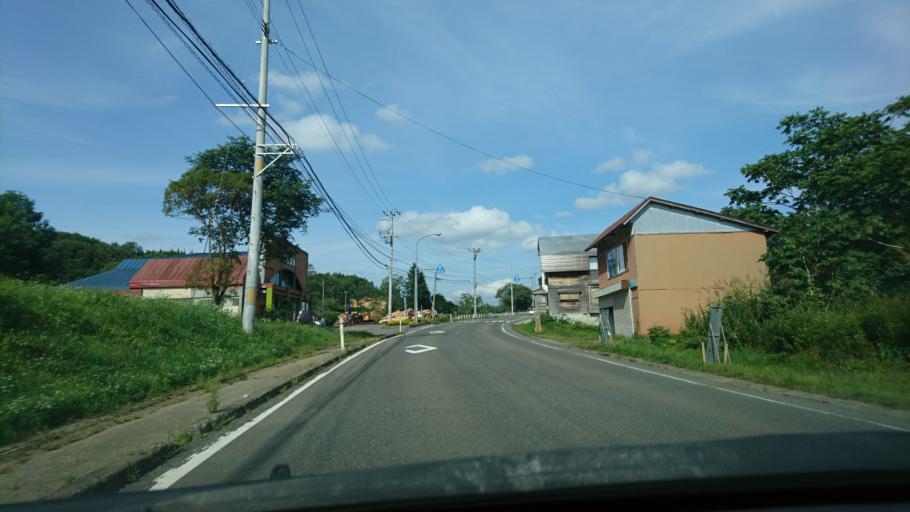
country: JP
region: Akita
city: Yokotemachi
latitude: 39.3000
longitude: 140.7363
